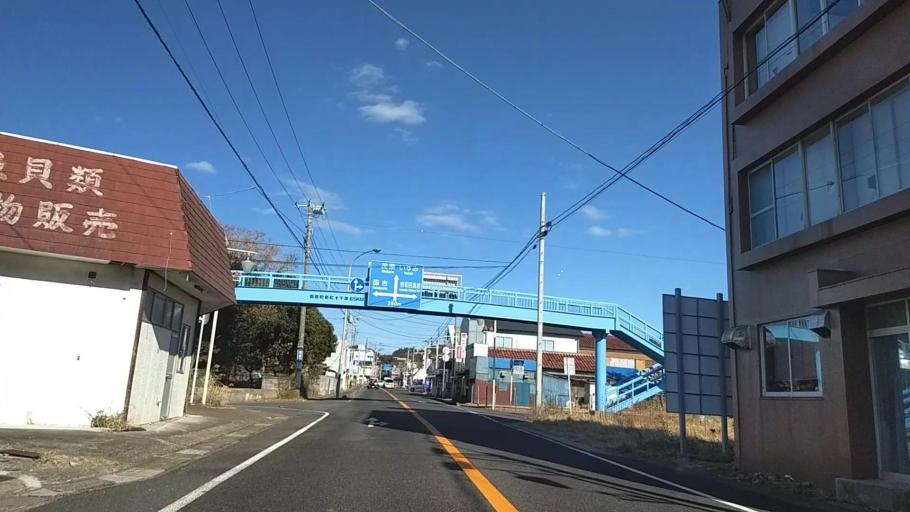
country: JP
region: Chiba
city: Katsuura
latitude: 35.1872
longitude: 140.3559
